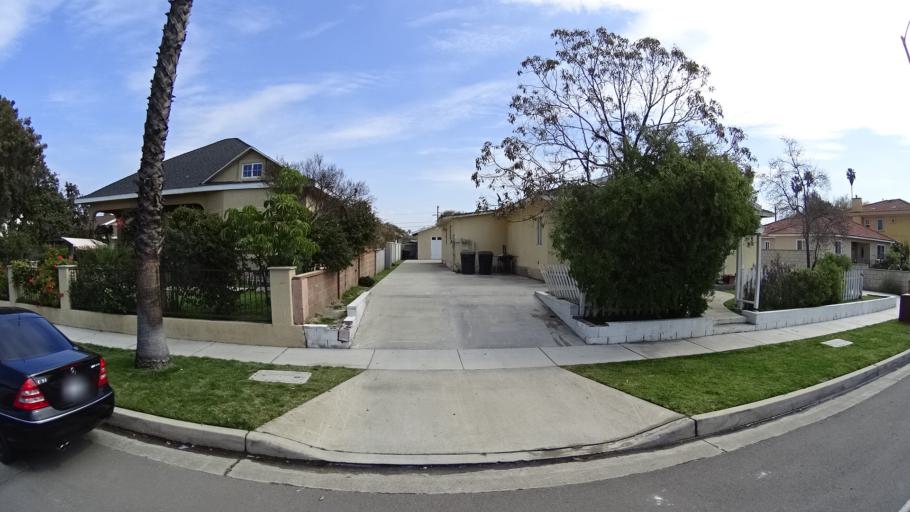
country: US
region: California
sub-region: Orange County
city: Anaheim
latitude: 33.8428
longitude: -117.9305
